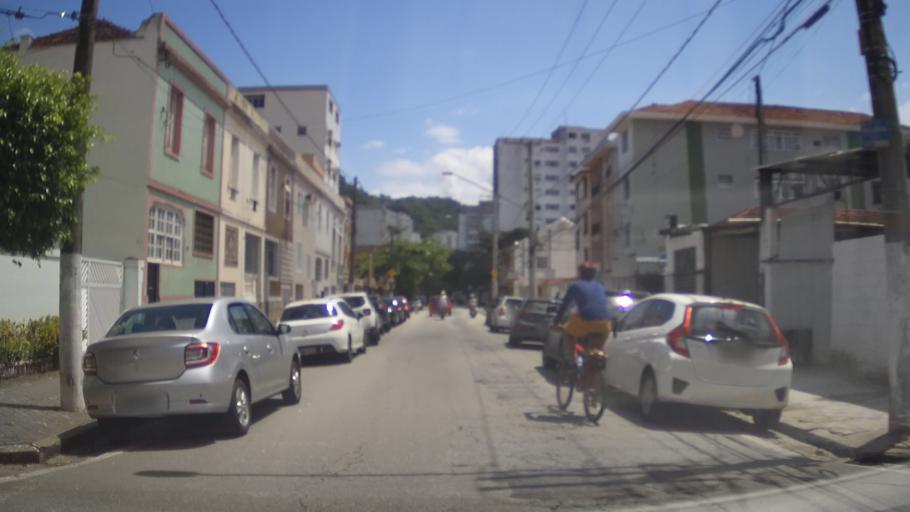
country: BR
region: Sao Paulo
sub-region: Santos
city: Santos
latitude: -23.9590
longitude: -46.3404
